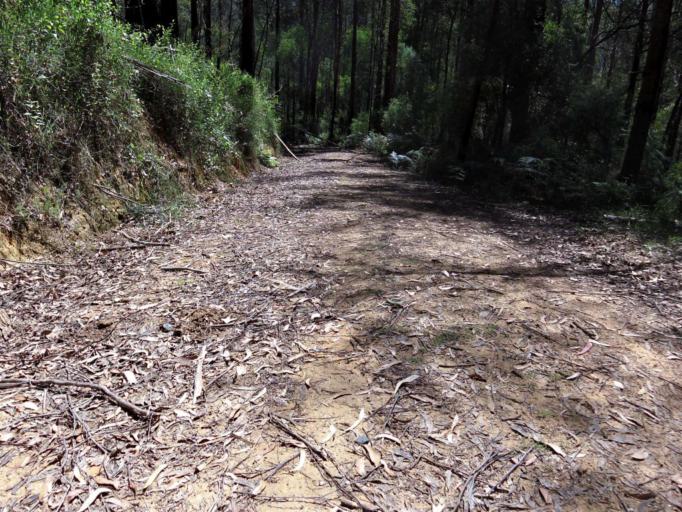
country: AU
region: Victoria
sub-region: Yarra Ranges
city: Millgrove
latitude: -37.8529
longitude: 145.7586
